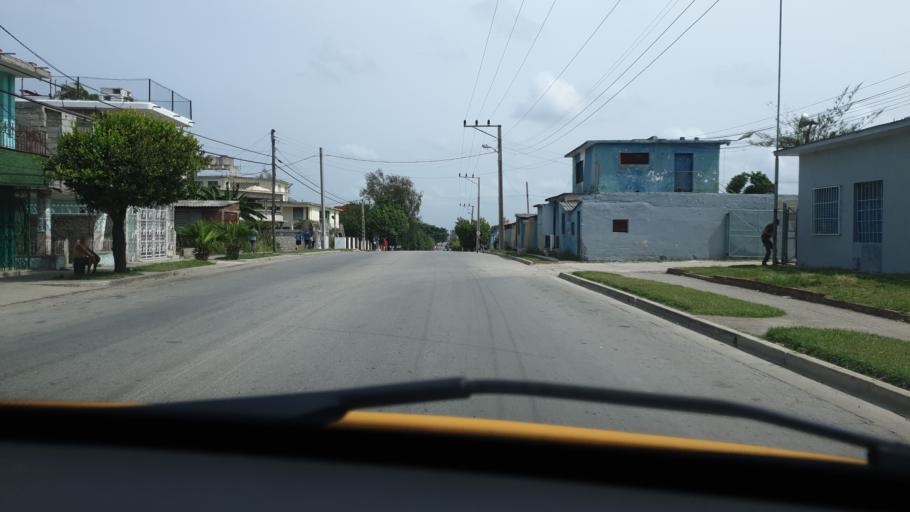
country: CU
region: Villa Clara
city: Santa Clara
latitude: 22.3902
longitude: -79.9601
